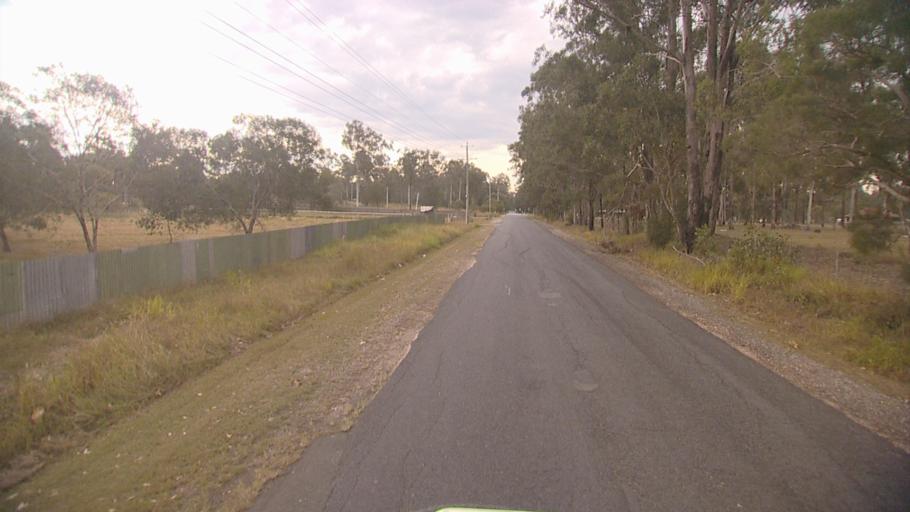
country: AU
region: Queensland
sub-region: Logan
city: Chambers Flat
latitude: -27.7723
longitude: 153.1158
